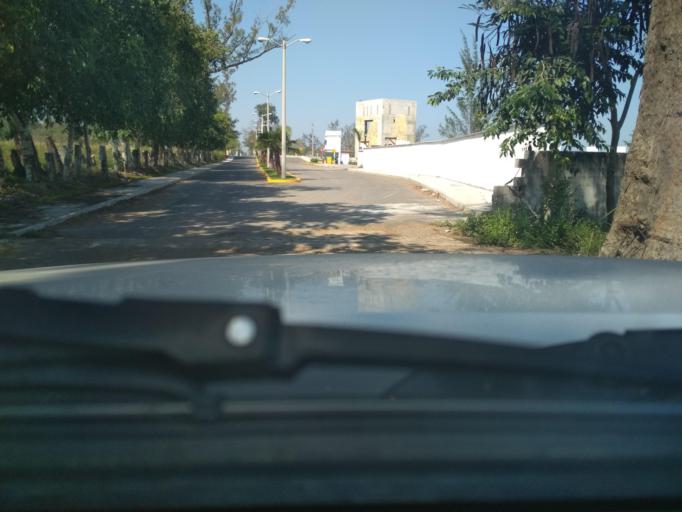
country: MX
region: Veracruz
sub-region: Veracruz
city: Las Amapolas
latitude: 19.1489
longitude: -96.2109
